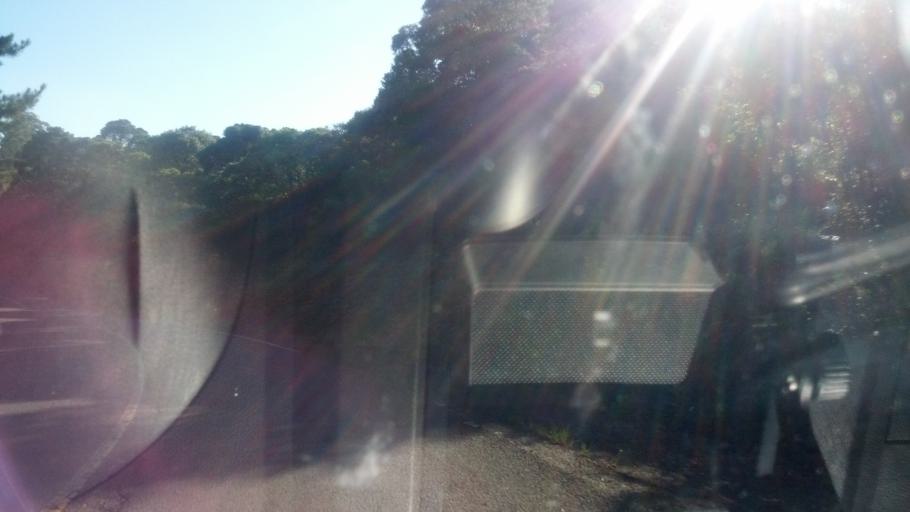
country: BR
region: Santa Catarina
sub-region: Lages
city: Lages
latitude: -27.9266
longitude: -50.5486
